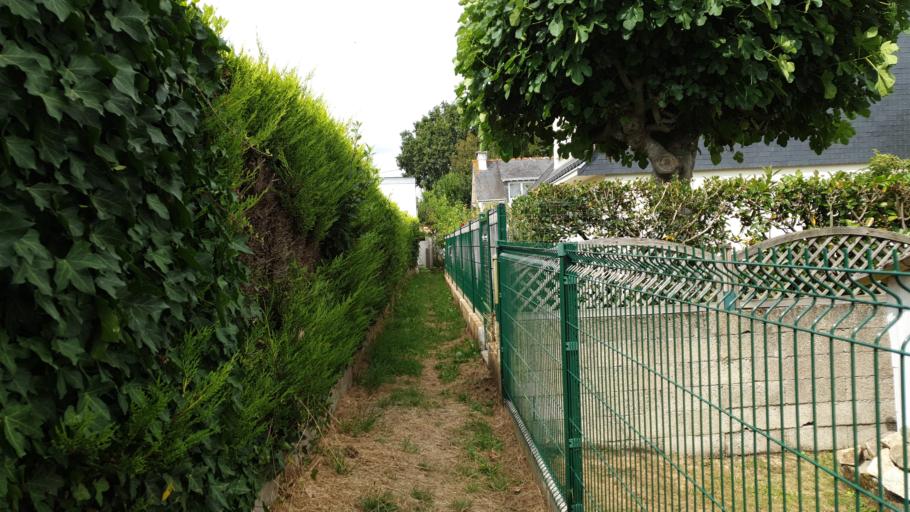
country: FR
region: Brittany
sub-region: Departement du Morbihan
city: Vannes
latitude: 47.6409
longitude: -2.7640
